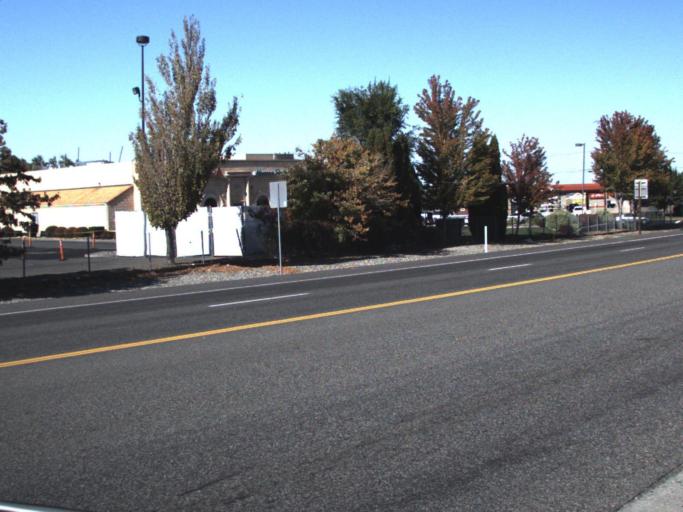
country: US
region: Washington
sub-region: Benton County
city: Kennewick
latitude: 46.1975
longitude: -119.1597
